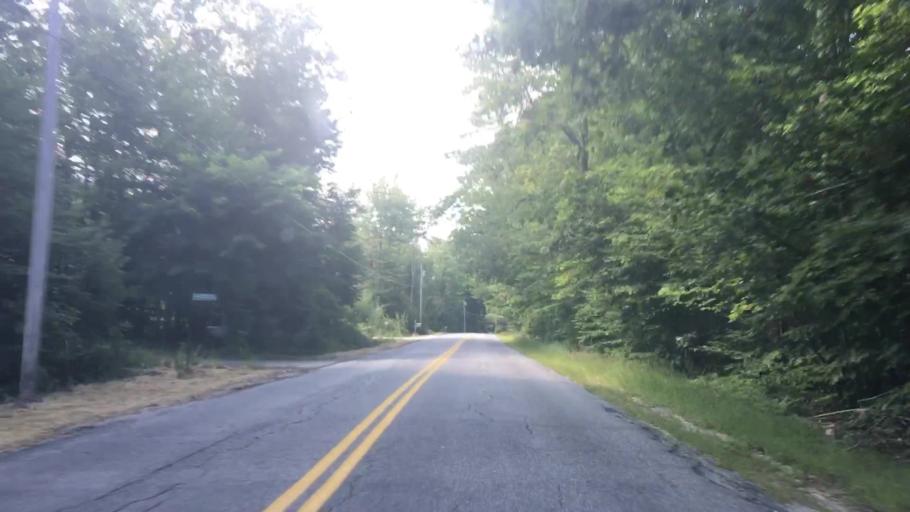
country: US
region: Maine
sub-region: Androscoggin County
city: Poland
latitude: 44.0147
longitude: -70.4187
